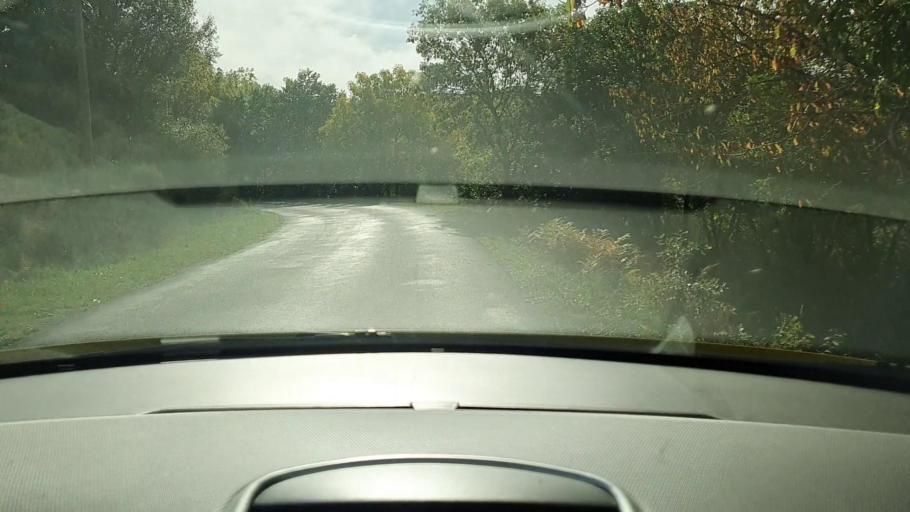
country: FR
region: Languedoc-Roussillon
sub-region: Departement de la Lozere
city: Meyrueis
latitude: 44.0691
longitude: 3.4568
